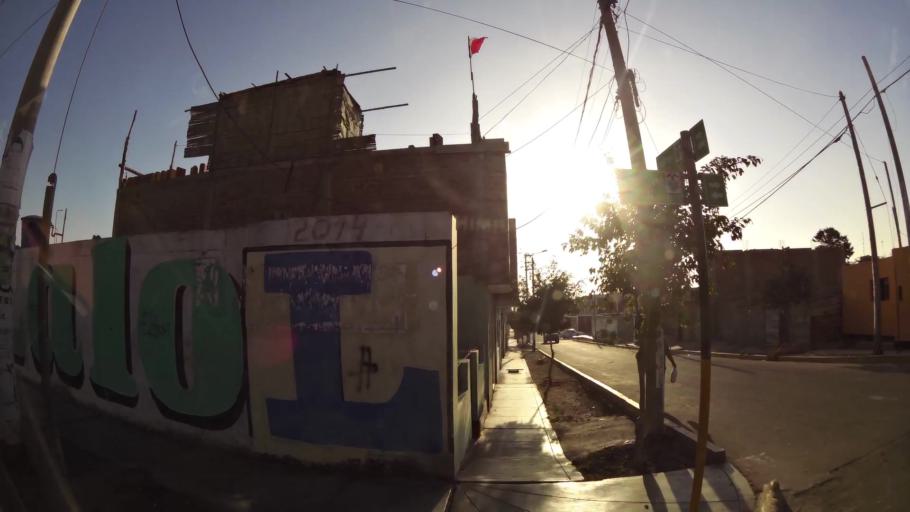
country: PE
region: Ica
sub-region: Provincia de Pisco
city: Villa Tupac Amaru
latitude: -13.7149
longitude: -76.1501
